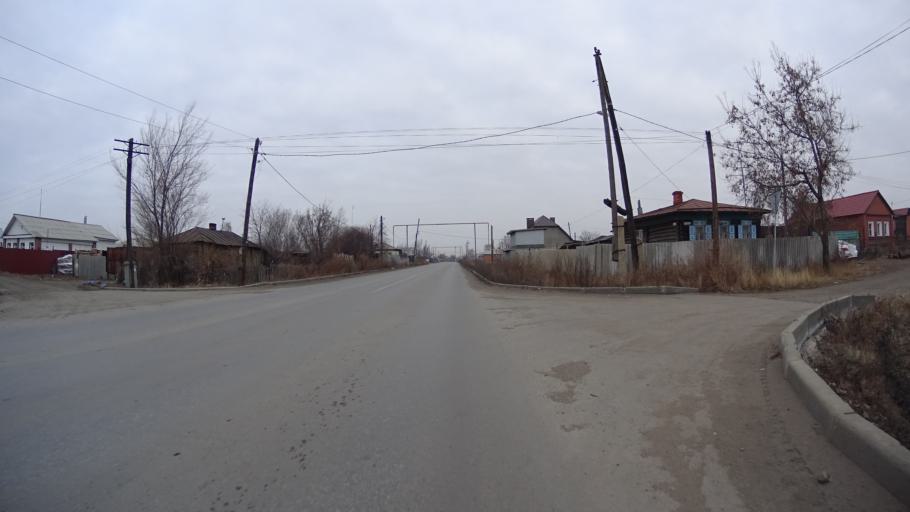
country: RU
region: Chelyabinsk
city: Troitsk
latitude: 54.1054
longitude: 61.5649
